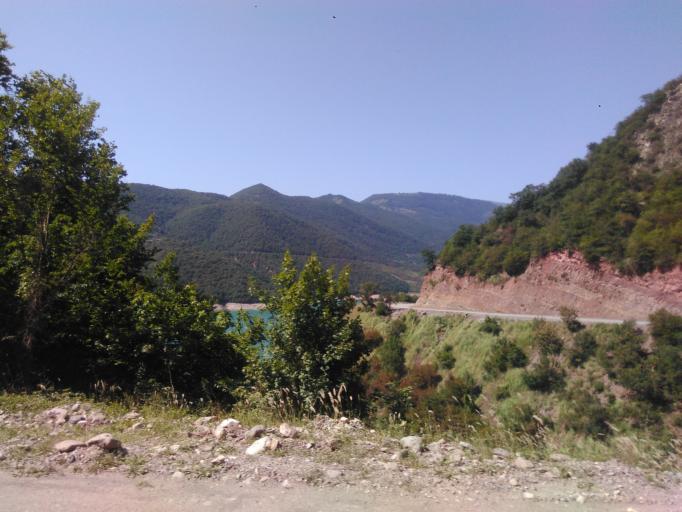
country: GE
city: Zhinvali
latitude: 42.1568
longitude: 44.7927
